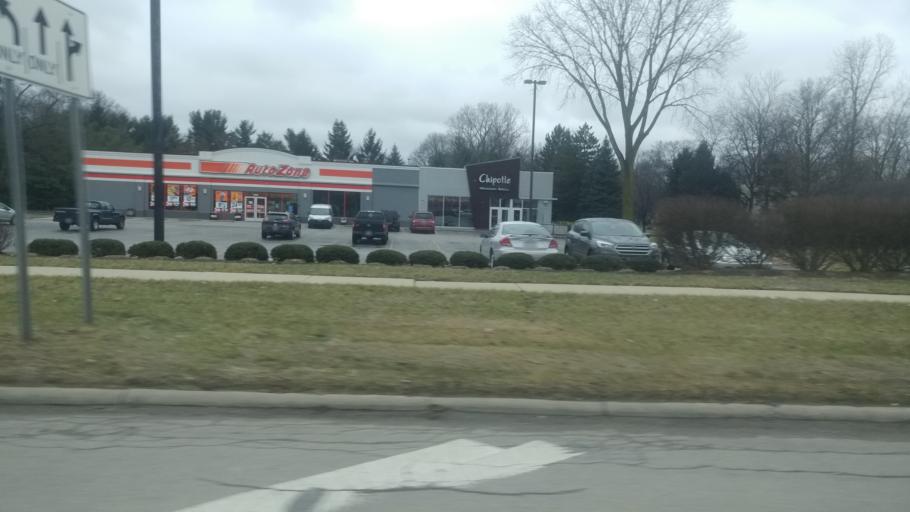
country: US
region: Ohio
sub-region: Lucas County
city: Sylvania
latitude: 41.6737
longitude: -83.7163
